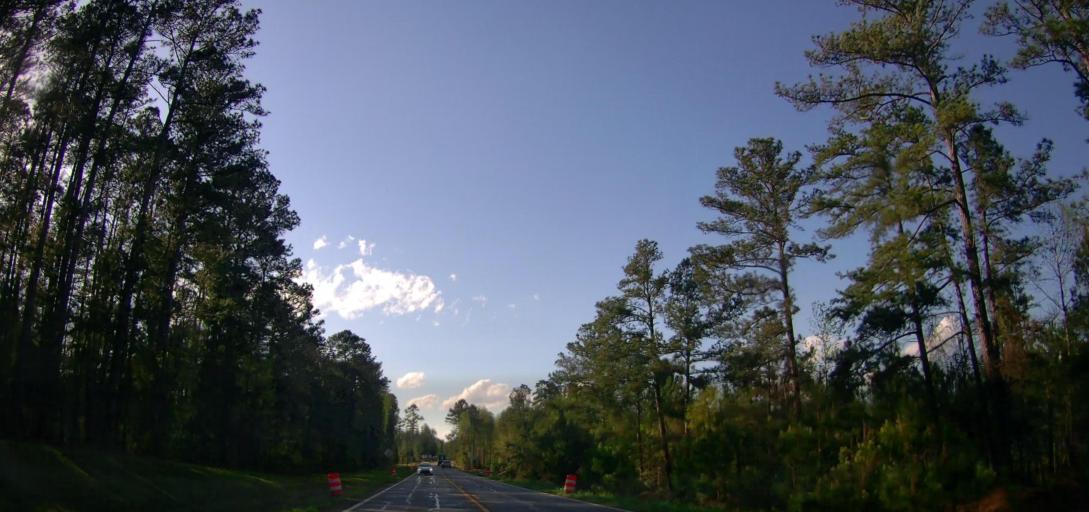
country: US
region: Georgia
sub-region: Baldwin County
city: Milledgeville
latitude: 33.1232
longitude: -83.2945
